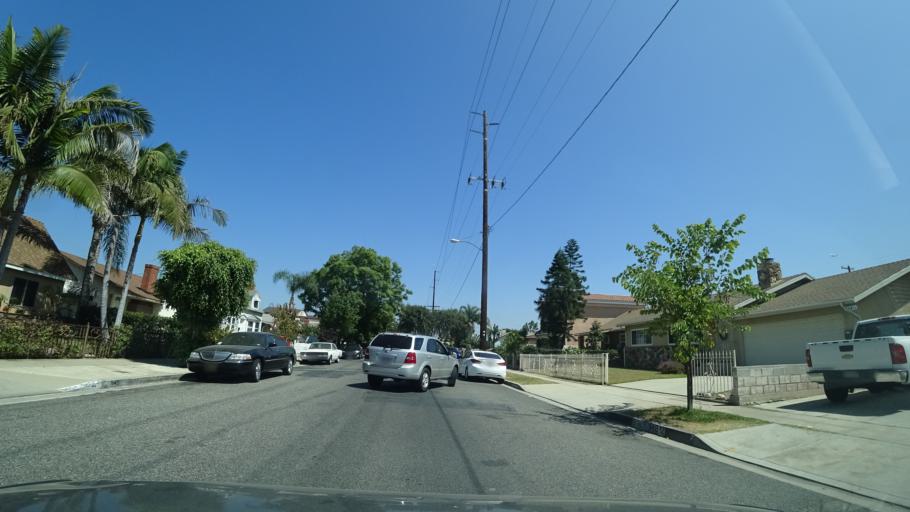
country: US
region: California
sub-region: Los Angeles County
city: Inglewood
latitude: 33.9509
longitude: -118.3668
